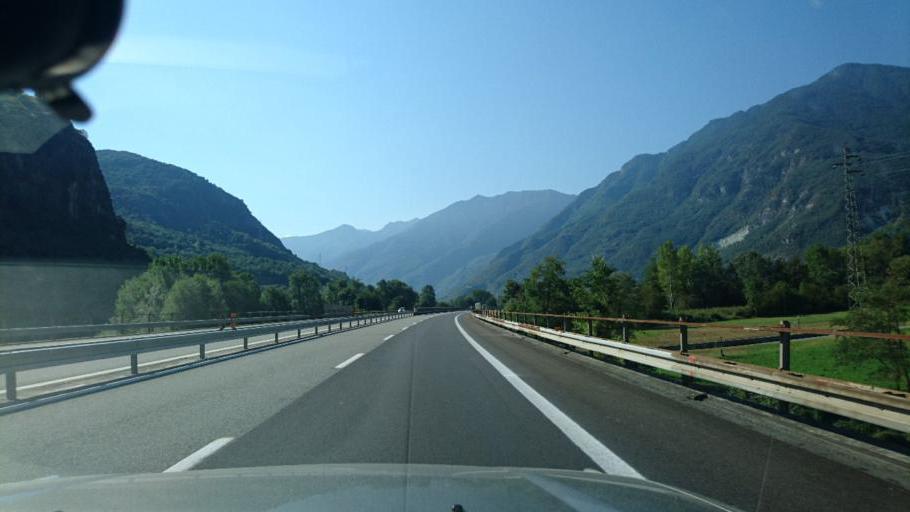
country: IT
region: Aosta Valley
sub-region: Valle d'Aosta
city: Montjovet
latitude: 45.6971
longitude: 7.6684
